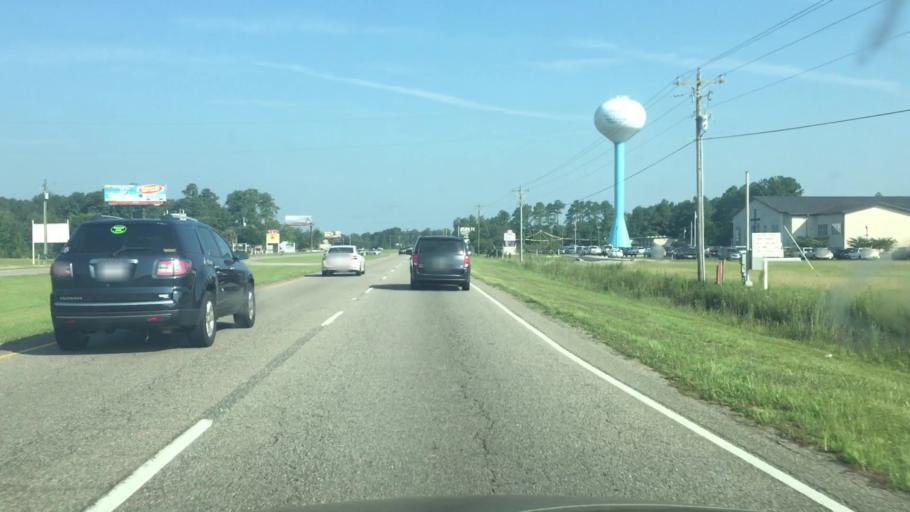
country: US
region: South Carolina
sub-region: Horry County
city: North Myrtle Beach
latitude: 33.9000
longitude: -78.6989
